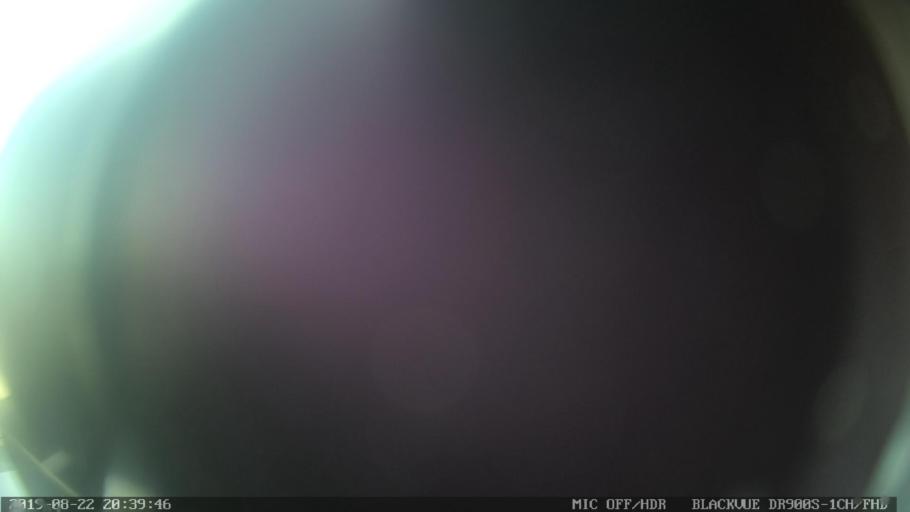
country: PT
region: Castelo Branco
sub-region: Proenca-A-Nova
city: Proenca-a-Nova
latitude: 39.6879
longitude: -7.7771
